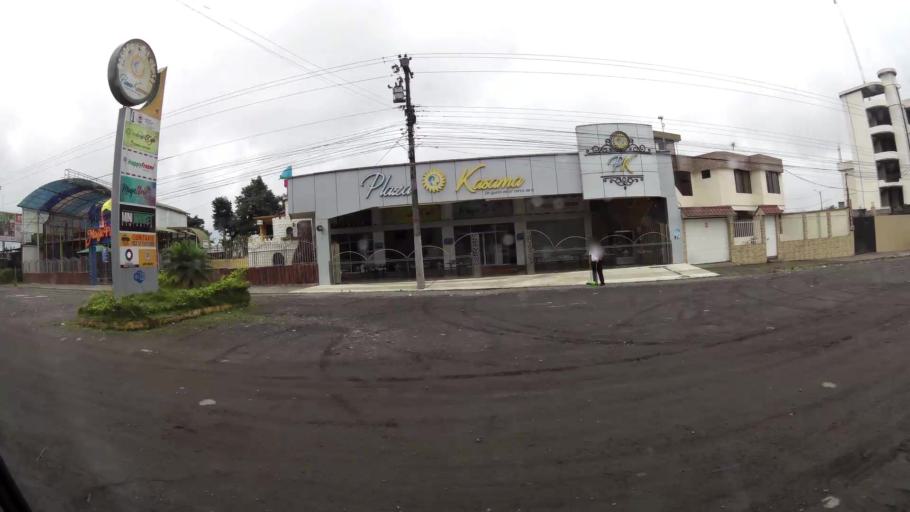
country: EC
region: Santo Domingo de los Tsachilas
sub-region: Canton Santo Domingo de los Colorados
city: Santo Domingo de los Colorados
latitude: -0.2485
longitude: -79.1425
